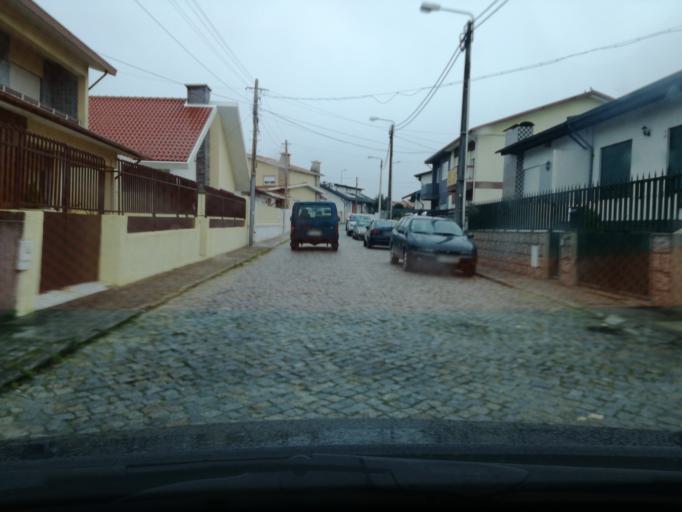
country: PT
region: Porto
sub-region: Maia
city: Gemunde
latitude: 41.2577
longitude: -8.6637
